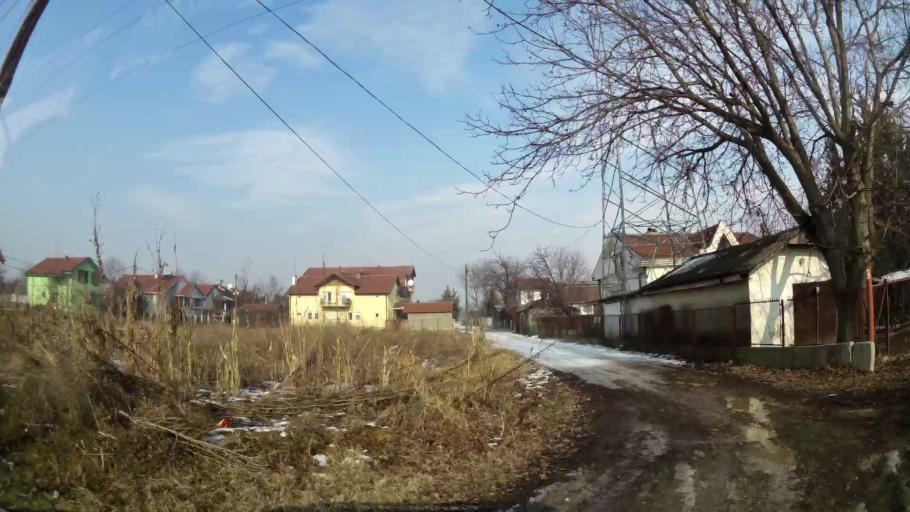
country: MK
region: Ilinden
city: Jurumleri
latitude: 41.9945
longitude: 21.5186
